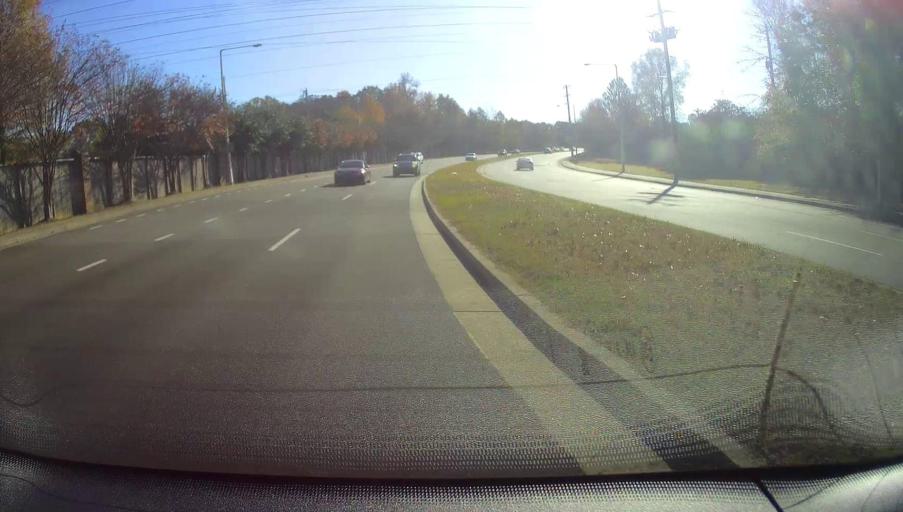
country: US
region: Tennessee
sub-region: Shelby County
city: Germantown
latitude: 35.0821
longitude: -89.8402
